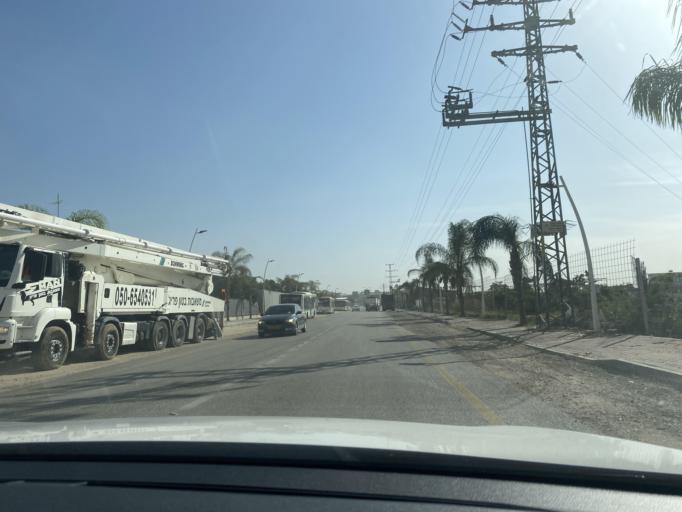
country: IL
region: Central District
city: Jaljulya
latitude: 32.1370
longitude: 34.9621
